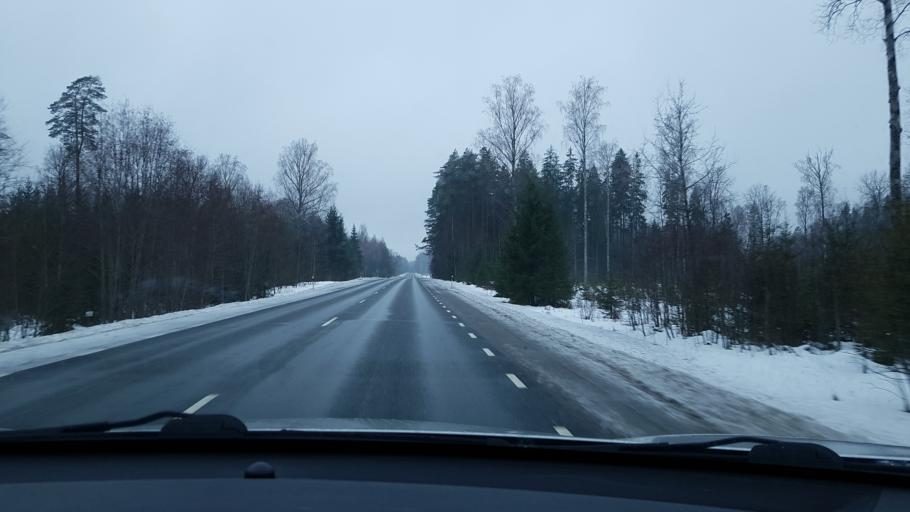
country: EE
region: Jaervamaa
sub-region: Tueri vald
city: Sarevere
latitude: 58.8055
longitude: 25.3098
